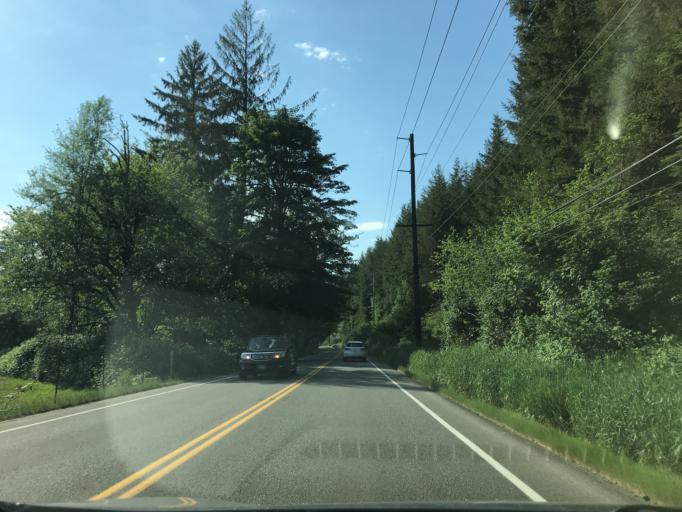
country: US
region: Washington
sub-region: King County
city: Hobart
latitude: 47.4403
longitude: -121.9819
